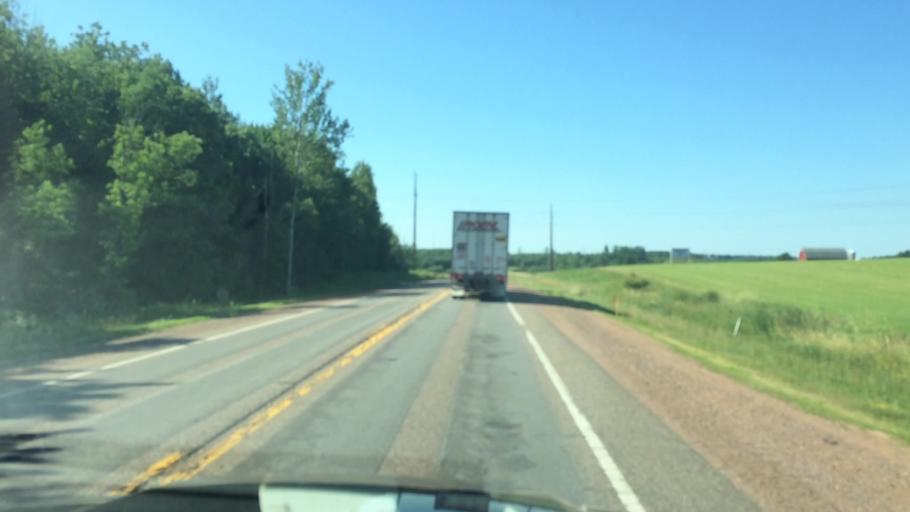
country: US
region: Wisconsin
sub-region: Marathon County
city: Athens
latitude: 44.9371
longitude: -90.0791
